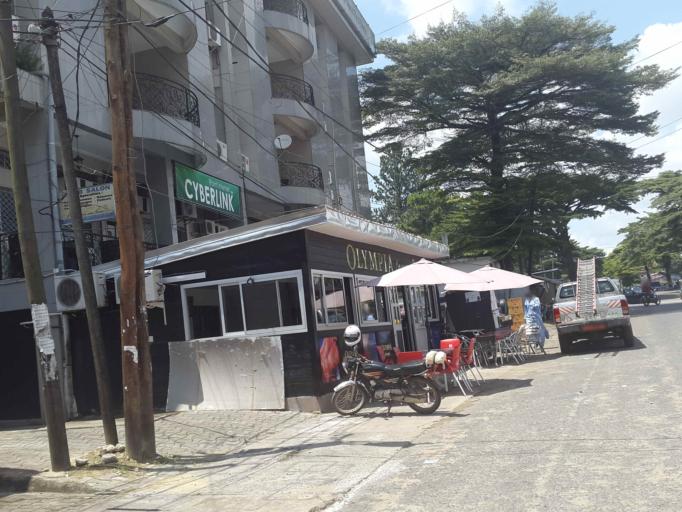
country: CM
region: Littoral
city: Douala
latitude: 4.0901
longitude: 9.7362
